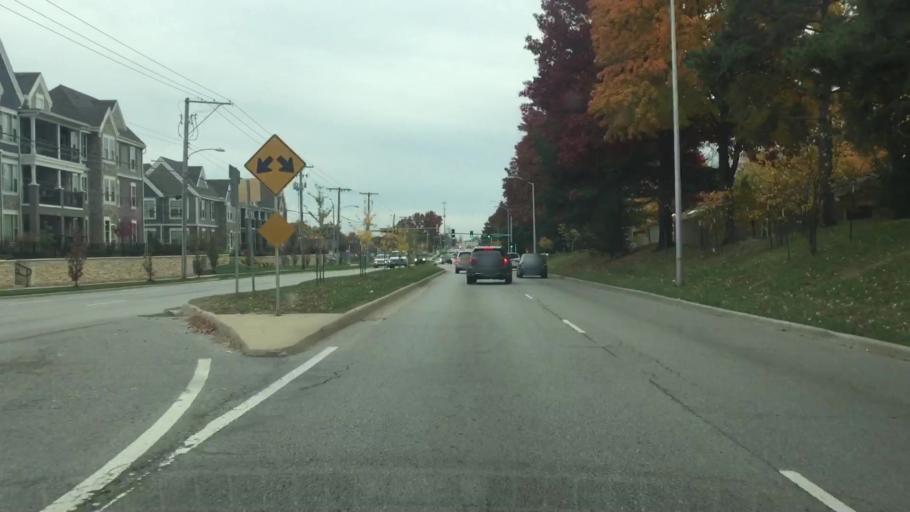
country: US
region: Kansas
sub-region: Johnson County
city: Lenexa
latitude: 38.9799
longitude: -94.7237
